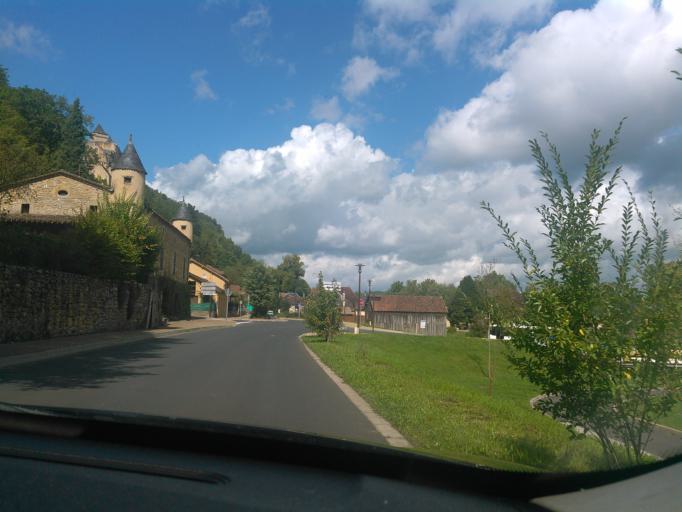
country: FR
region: Aquitaine
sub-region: Departement de la Dordogne
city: Cenac-et-Saint-Julien
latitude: 44.8121
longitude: 1.1523
